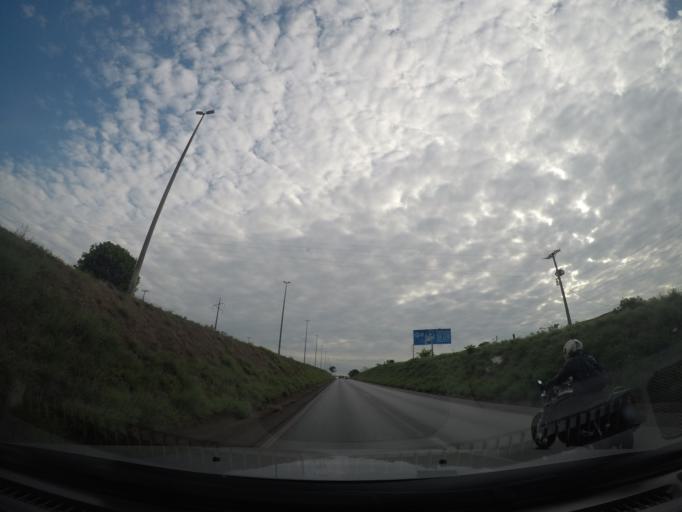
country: BR
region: Goias
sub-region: Planaltina
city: Planaltina
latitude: -15.6059
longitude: -47.6892
